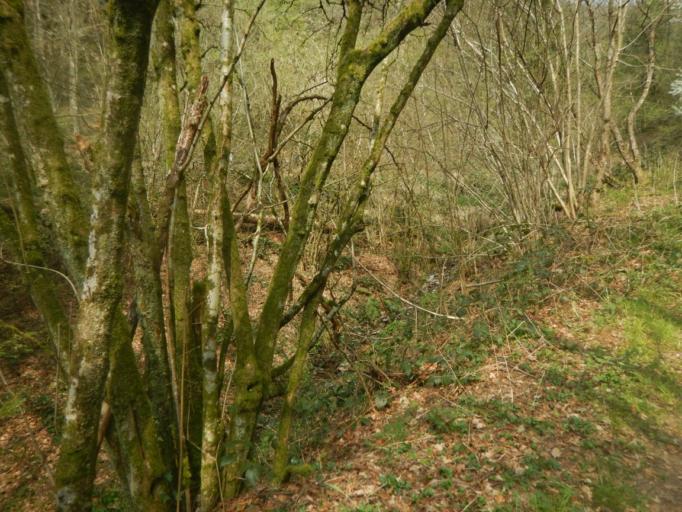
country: LU
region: Diekirch
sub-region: Canton de Wiltz
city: Esch-sur-Sure
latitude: 49.9167
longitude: 5.9172
